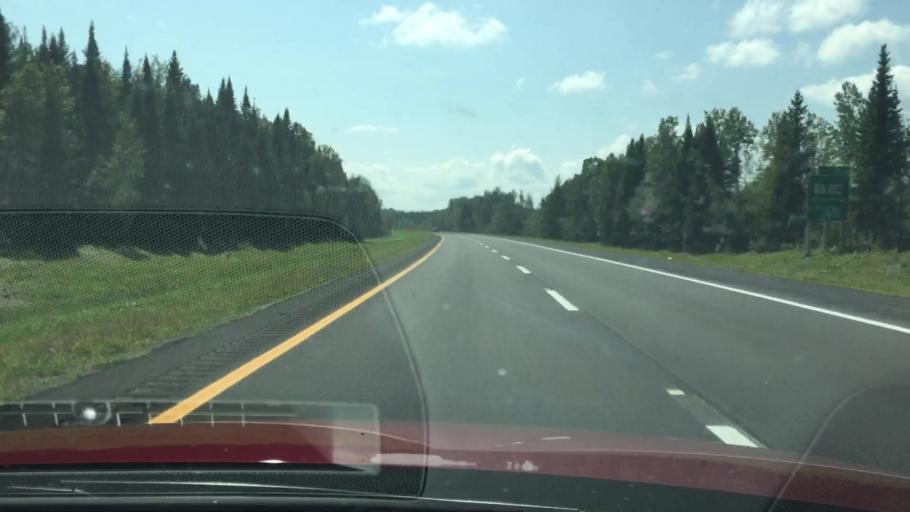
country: US
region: Maine
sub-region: Penobscot County
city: Patten
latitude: 45.8905
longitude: -68.4039
